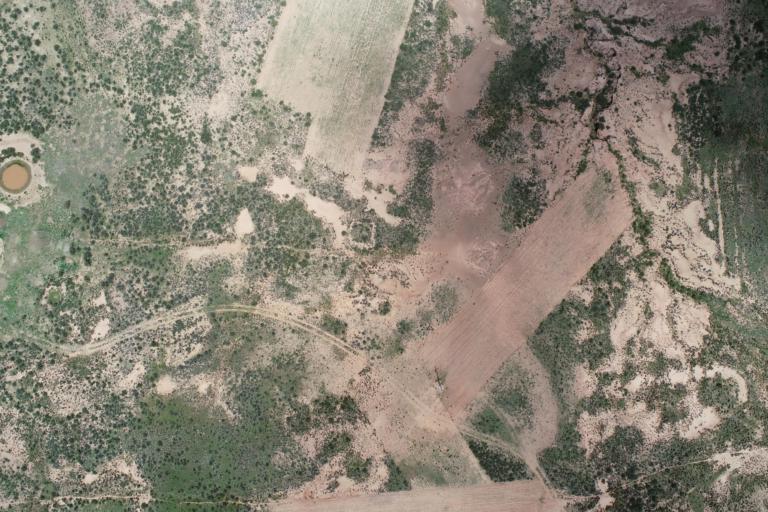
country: BO
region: La Paz
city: Curahuara de Carangas
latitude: -17.3237
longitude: -68.4987
